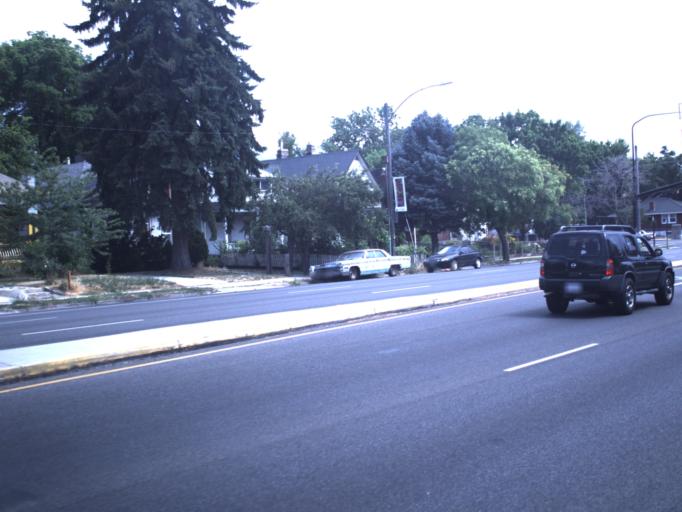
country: US
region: Utah
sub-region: Salt Lake County
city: Salt Lake City
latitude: 40.7529
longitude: -111.8712
